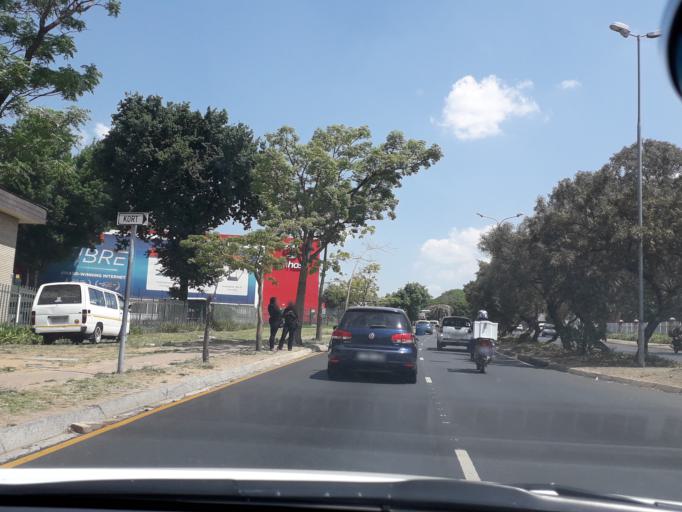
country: ZA
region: Gauteng
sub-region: City of Johannesburg Metropolitan Municipality
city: Midrand
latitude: -26.0451
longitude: 28.0597
